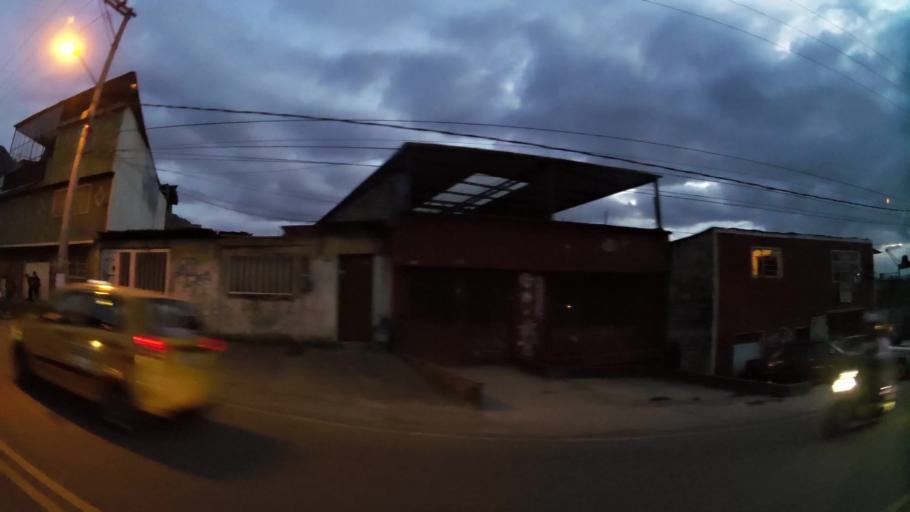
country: CO
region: Bogota D.C.
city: Bogota
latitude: 4.5489
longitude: -74.0848
